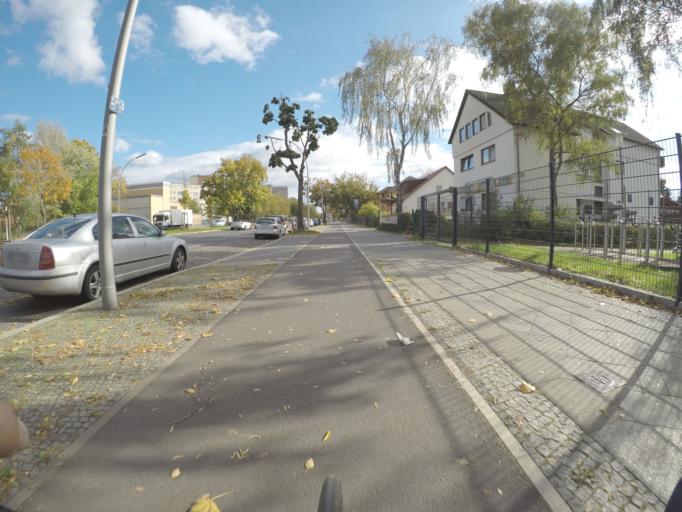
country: DE
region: Berlin
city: Falkenhagener Feld
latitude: 52.5501
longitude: 13.1704
